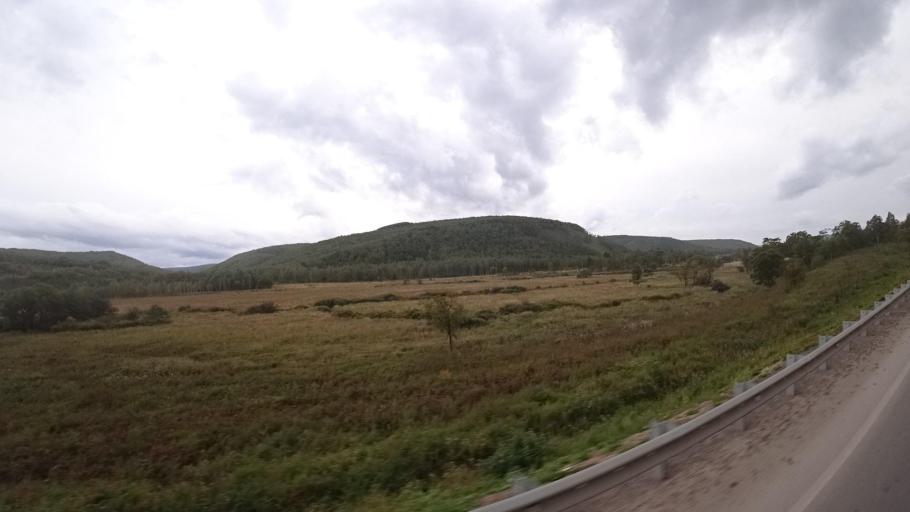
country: RU
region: Jewish Autonomous Oblast
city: Khingansk
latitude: 48.9908
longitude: 131.1197
